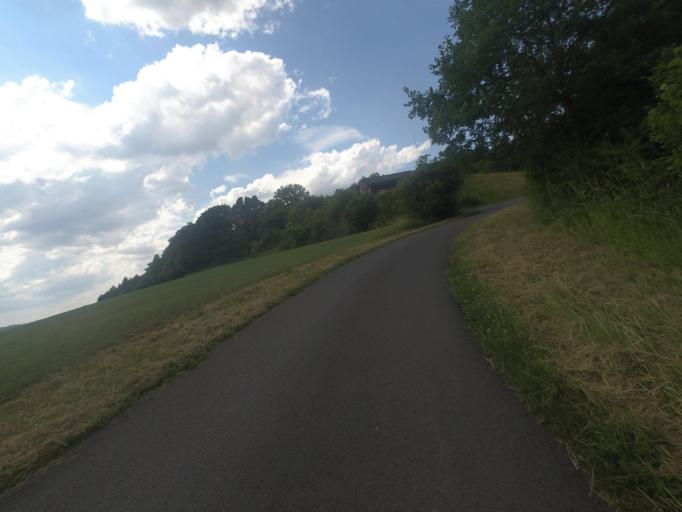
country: DE
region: Rheinland-Pfalz
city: Gerolstein
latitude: 50.2317
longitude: 6.6350
